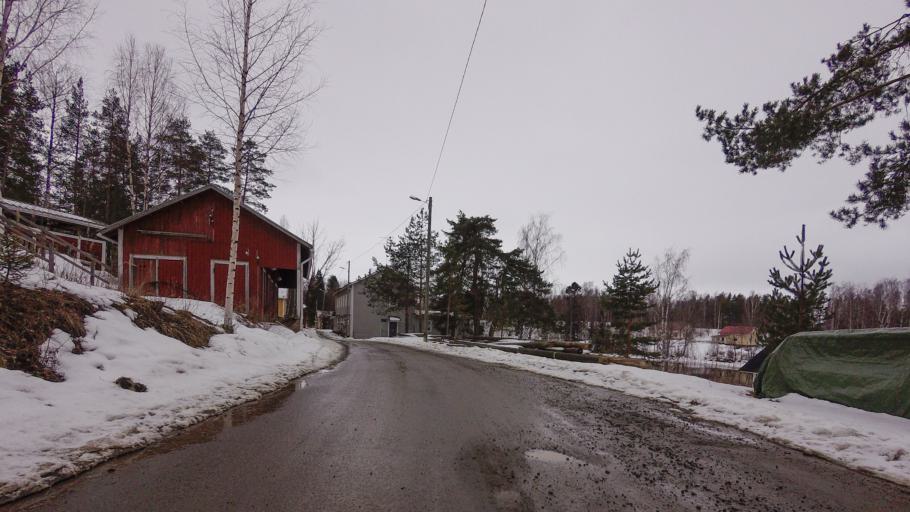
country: FI
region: Southern Savonia
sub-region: Savonlinna
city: Rantasalmi
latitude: 62.1143
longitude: 28.6079
